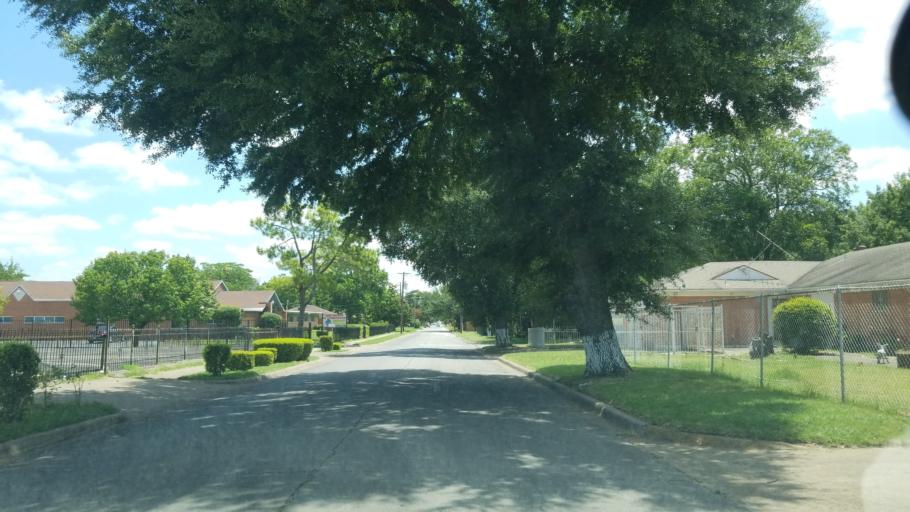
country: US
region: Texas
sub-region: Dallas County
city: Balch Springs
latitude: 32.7445
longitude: -96.6994
